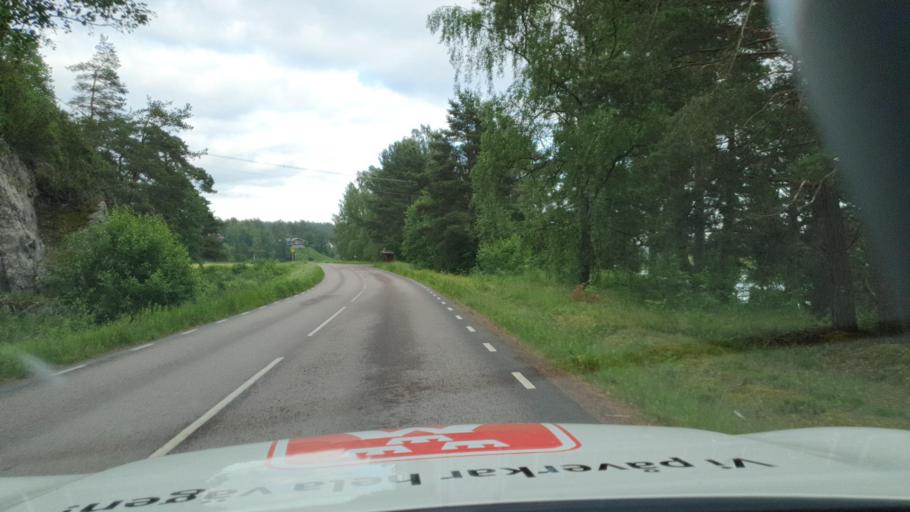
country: SE
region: Vaermland
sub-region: Karlstads Kommun
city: Karlstad
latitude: 59.4250
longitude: 13.4735
